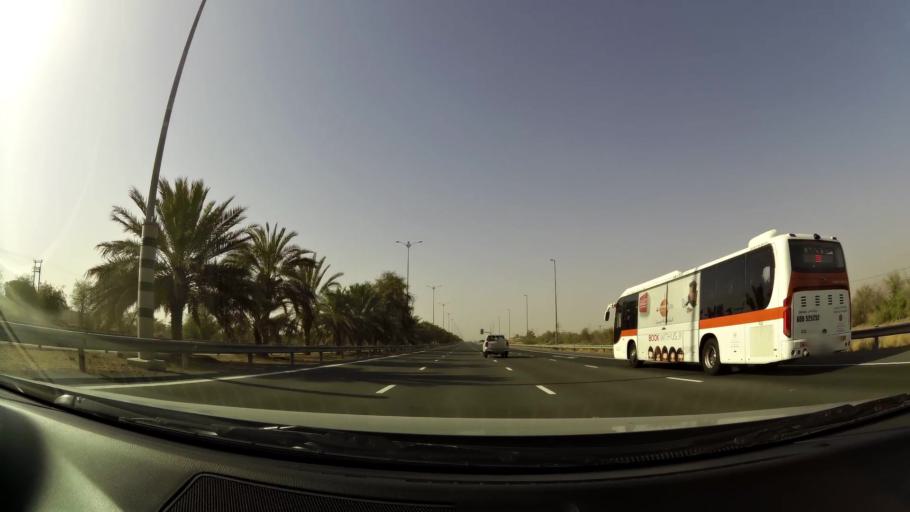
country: OM
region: Al Buraimi
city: Al Buraymi
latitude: 24.5262
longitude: 55.7608
